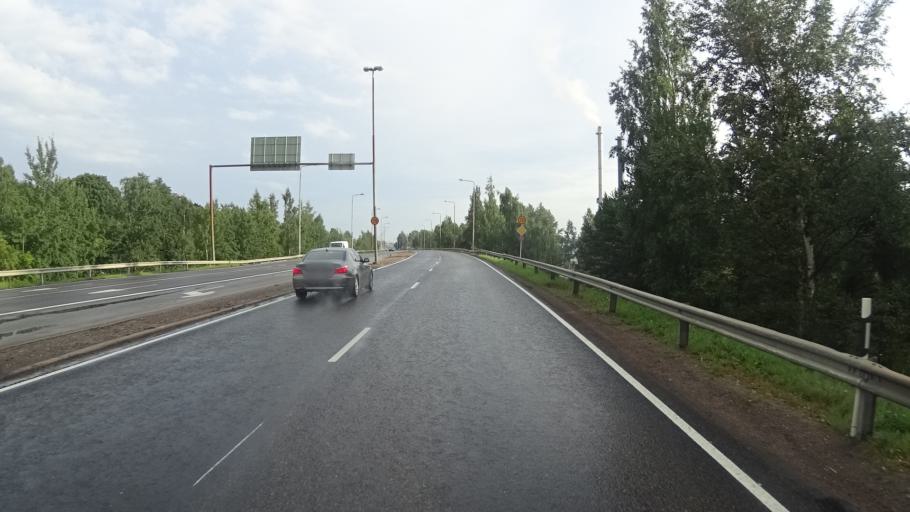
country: FI
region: Kymenlaakso
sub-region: Kotka-Hamina
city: Kotka
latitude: 60.4735
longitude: 26.9177
